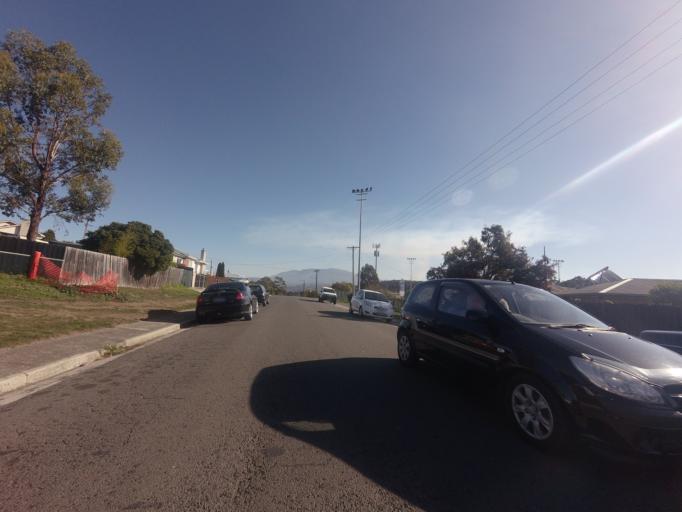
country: AU
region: Tasmania
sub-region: Clarence
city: Warrane
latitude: -42.8561
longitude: 147.3837
